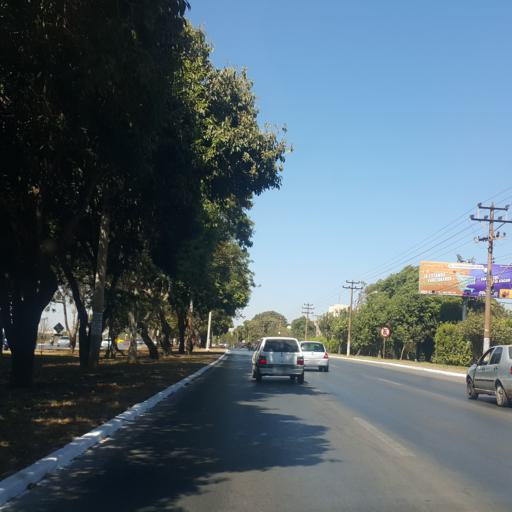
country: BR
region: Federal District
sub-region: Brasilia
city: Brasilia
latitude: -15.8078
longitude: -48.0586
